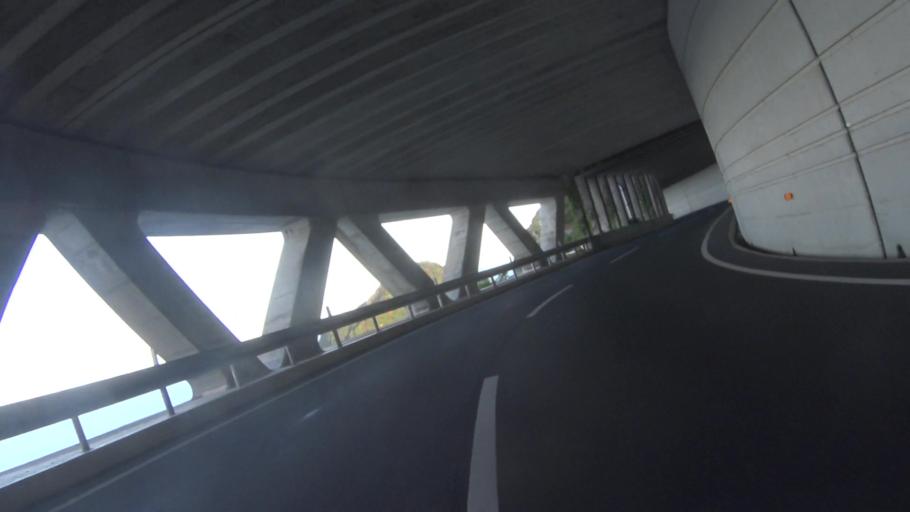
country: JP
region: Kyoto
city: Miyazu
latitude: 35.7597
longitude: 135.2417
